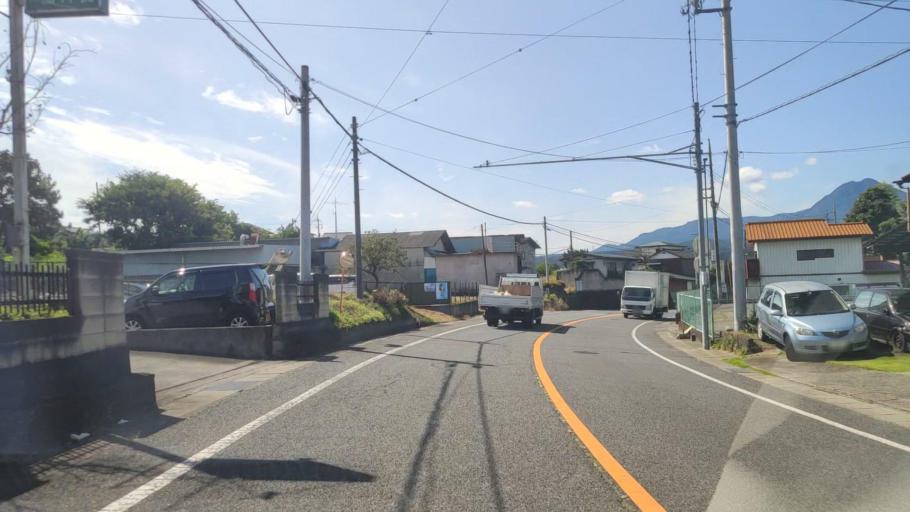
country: JP
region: Gunma
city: Shibukawa
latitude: 36.5183
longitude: 139.0097
